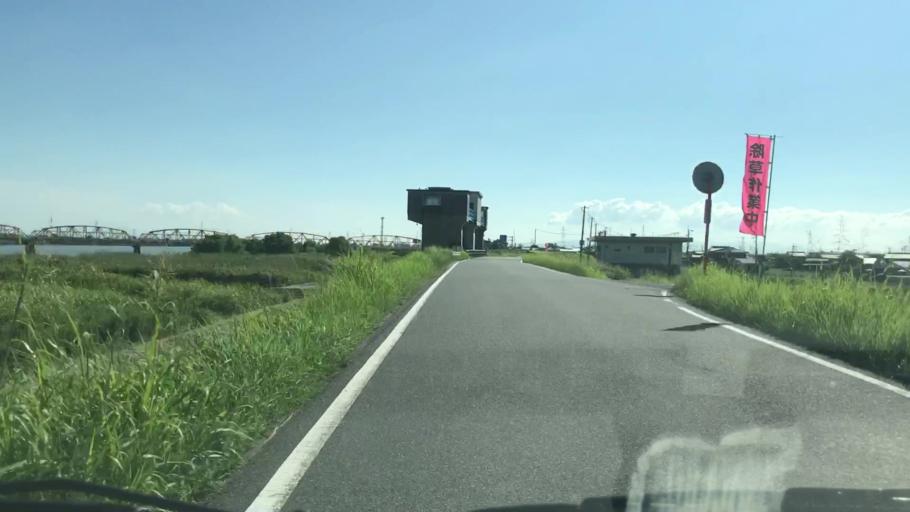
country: JP
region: Saga Prefecture
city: Kanzakimachi-kanzaki
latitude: 33.2649
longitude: 130.4194
